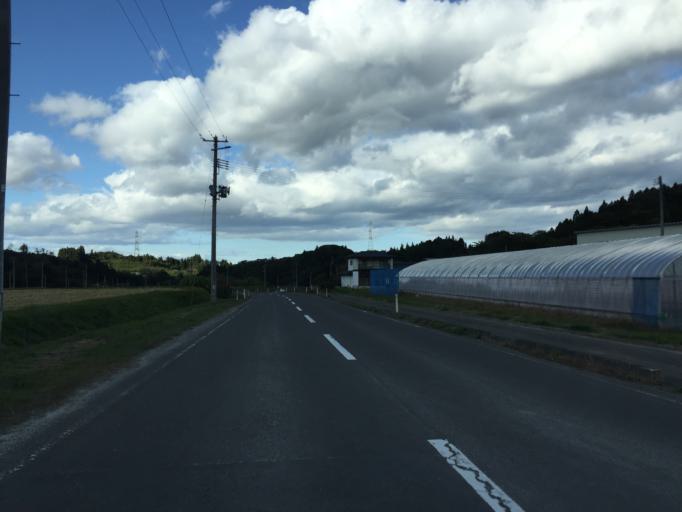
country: JP
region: Miyagi
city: Marumori
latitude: 37.8477
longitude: 140.8315
